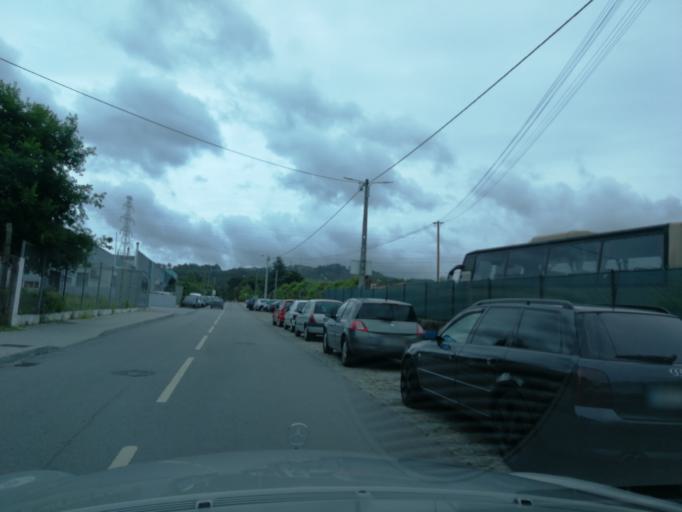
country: PT
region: Braga
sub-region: Braga
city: Adaufe
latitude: 41.6034
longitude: -8.3815
